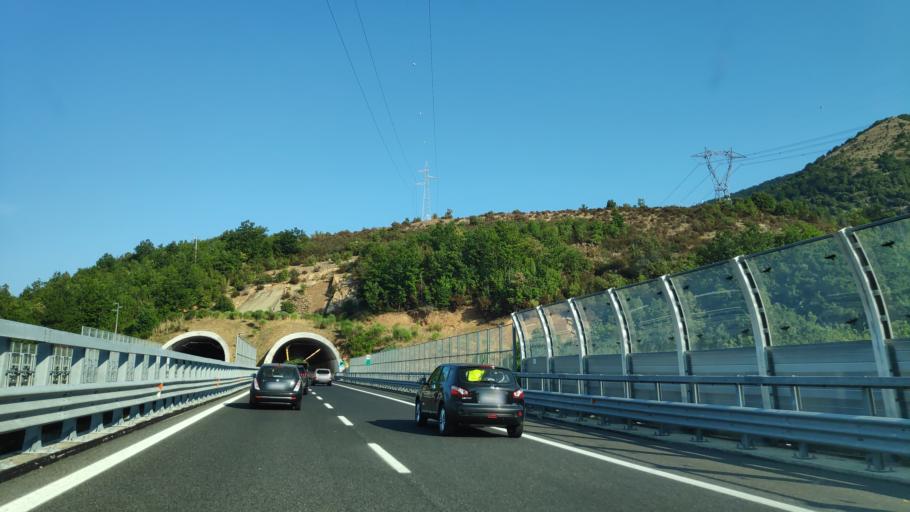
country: IT
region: Basilicate
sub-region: Provincia di Potenza
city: Lagonegro
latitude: 40.1249
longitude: 15.7797
